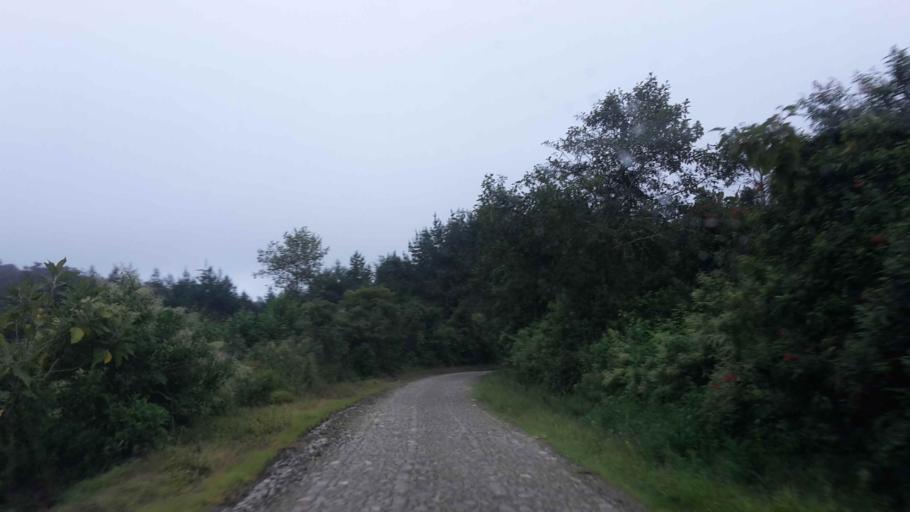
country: BO
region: Cochabamba
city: Colomi
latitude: -17.1312
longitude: -65.9498
